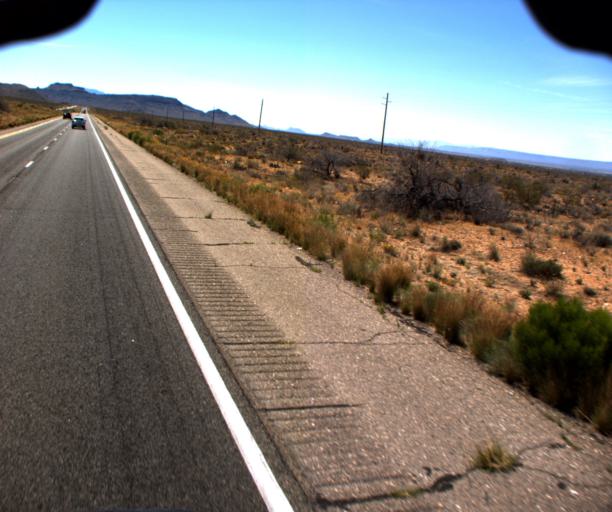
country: US
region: Arizona
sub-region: Mohave County
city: Golden Valley
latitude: 35.2718
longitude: -114.1690
